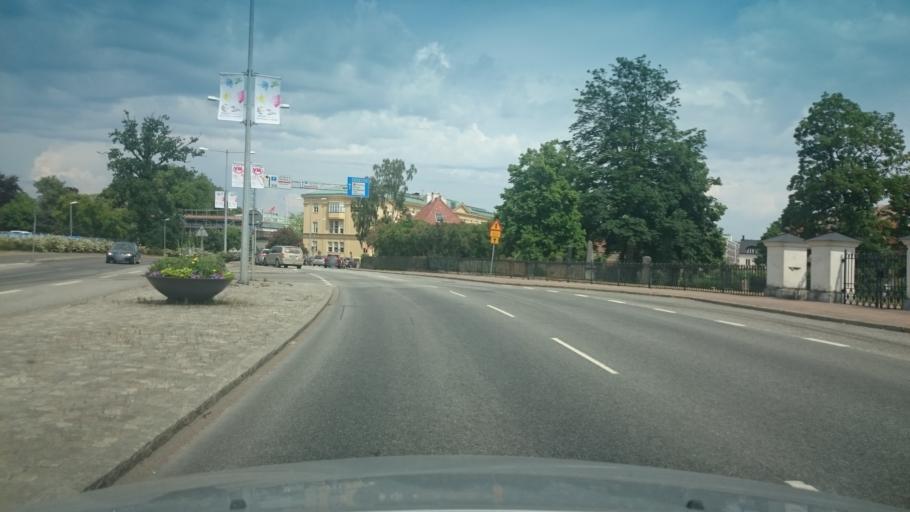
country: SE
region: Skane
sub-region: Kristianstads Kommun
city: Kristianstad
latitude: 56.0247
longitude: 14.1563
